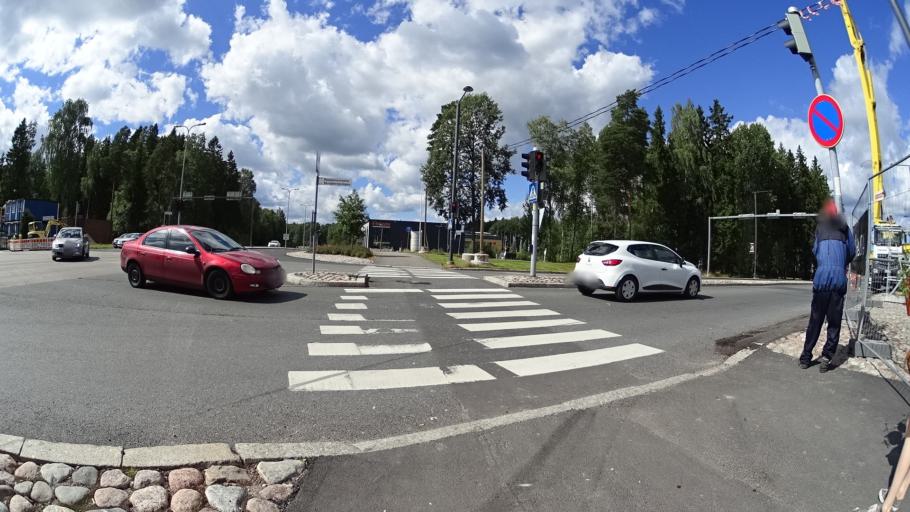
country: FI
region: Uusimaa
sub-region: Helsinki
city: Teekkarikylae
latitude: 60.2594
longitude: 24.8436
